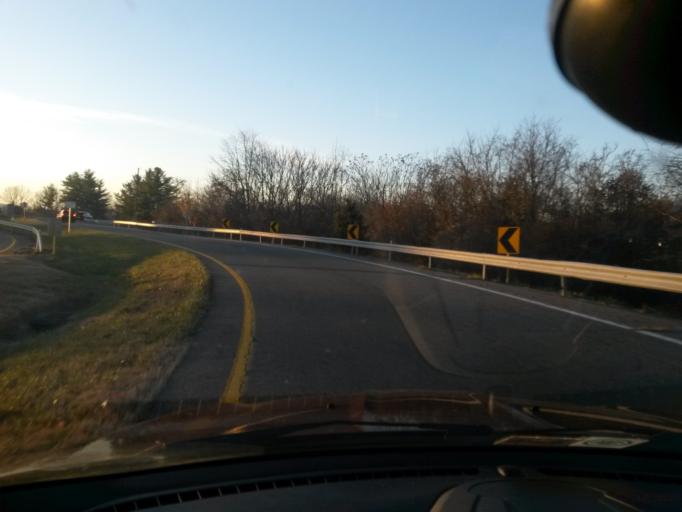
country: US
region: Virginia
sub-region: Roanoke County
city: Hollins
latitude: 37.3273
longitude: -79.9914
